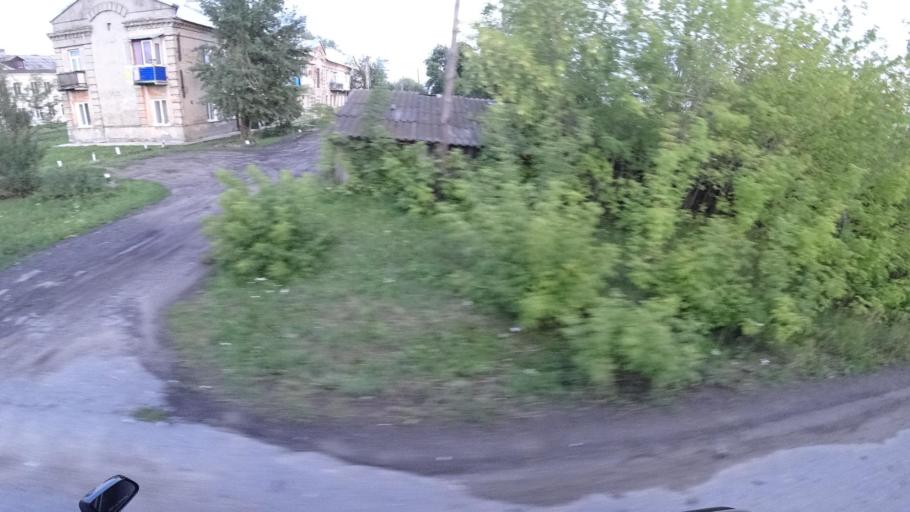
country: RU
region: Sverdlovsk
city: Kamyshlov
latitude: 56.8491
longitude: 62.7322
